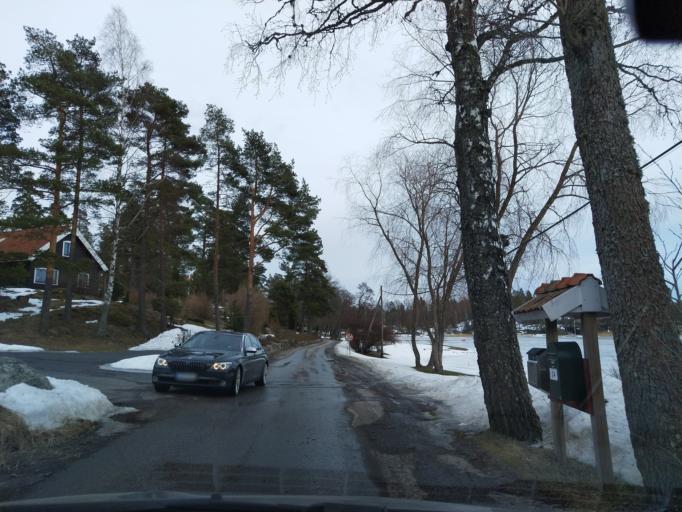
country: FI
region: Uusimaa
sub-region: Helsinki
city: Sibbo
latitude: 60.2568
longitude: 25.3035
